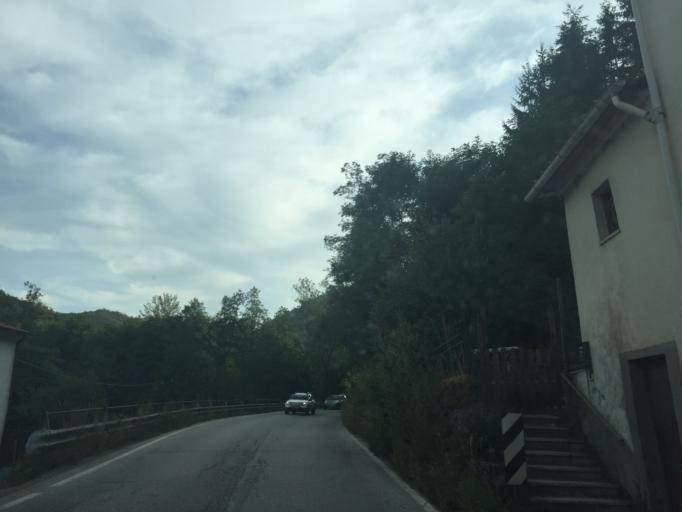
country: IT
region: Tuscany
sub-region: Provincia di Pistoia
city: Campo Tizzoro
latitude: 44.0128
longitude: 10.8572
